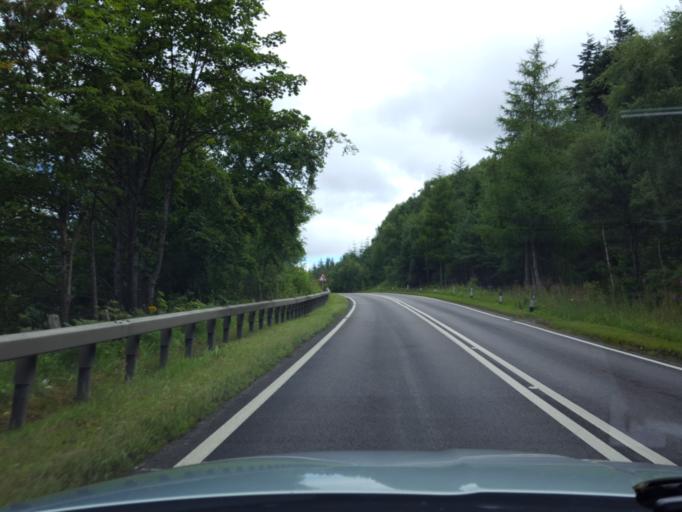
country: GB
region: Scotland
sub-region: Moray
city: Rothes
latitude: 57.4822
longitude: -3.1958
